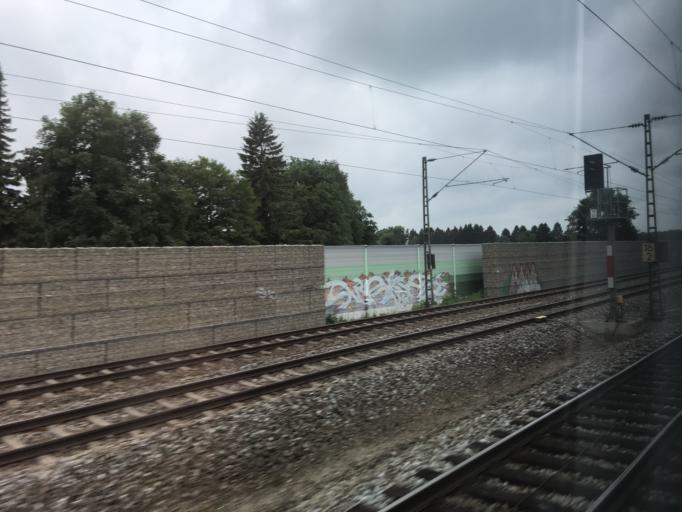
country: DE
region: Bavaria
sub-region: Upper Bavaria
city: Grobenzell
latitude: 48.1977
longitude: 11.3694
